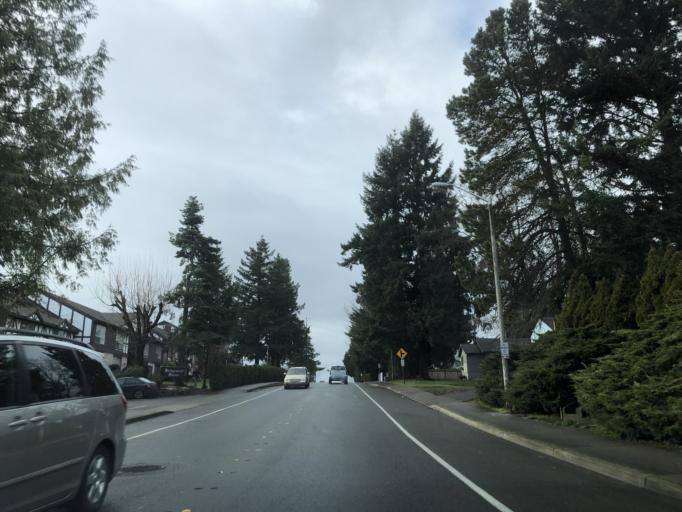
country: US
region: Washington
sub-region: King County
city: SeaTac
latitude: 47.4453
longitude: -122.2865
